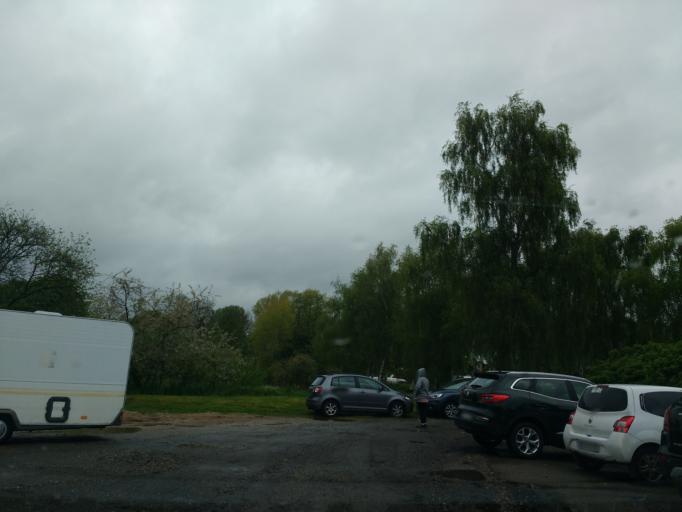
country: DE
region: Schleswig-Holstein
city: Loose
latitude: 54.4960
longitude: 9.9366
